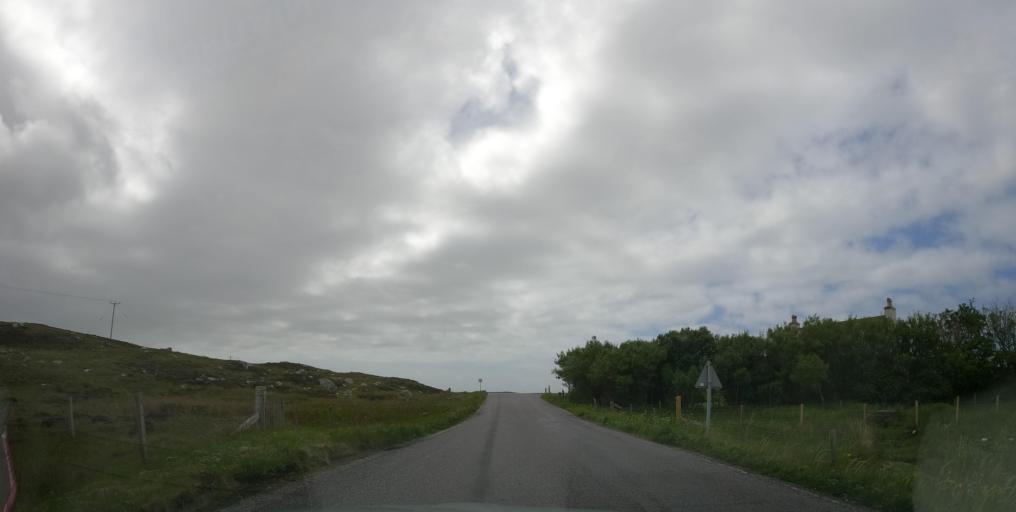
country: GB
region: Scotland
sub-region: Eilean Siar
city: Isle of South Uist
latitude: 57.2936
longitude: -7.3649
